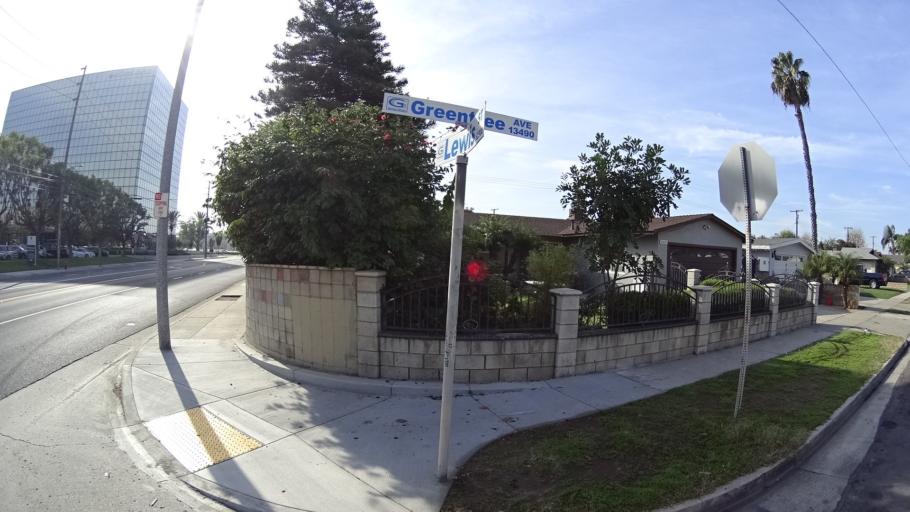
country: US
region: California
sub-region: Orange County
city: Orange
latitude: 33.7843
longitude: -117.8977
